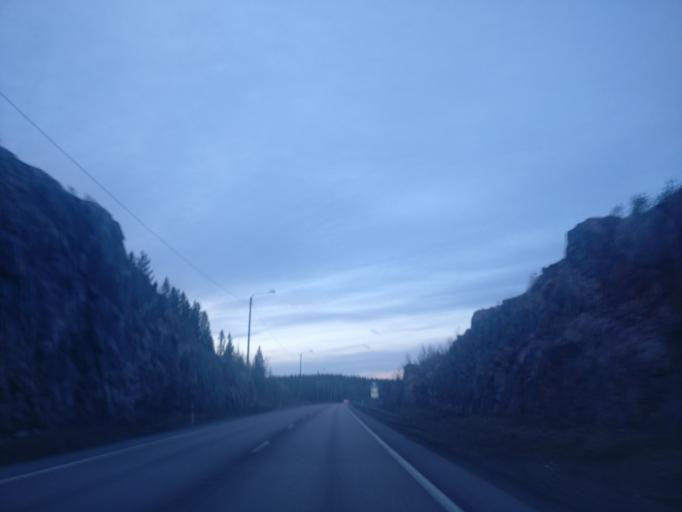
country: FI
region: Central Finland
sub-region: Jyvaeskylae
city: Saeynaetsalo
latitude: 62.2070
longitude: 25.8898
